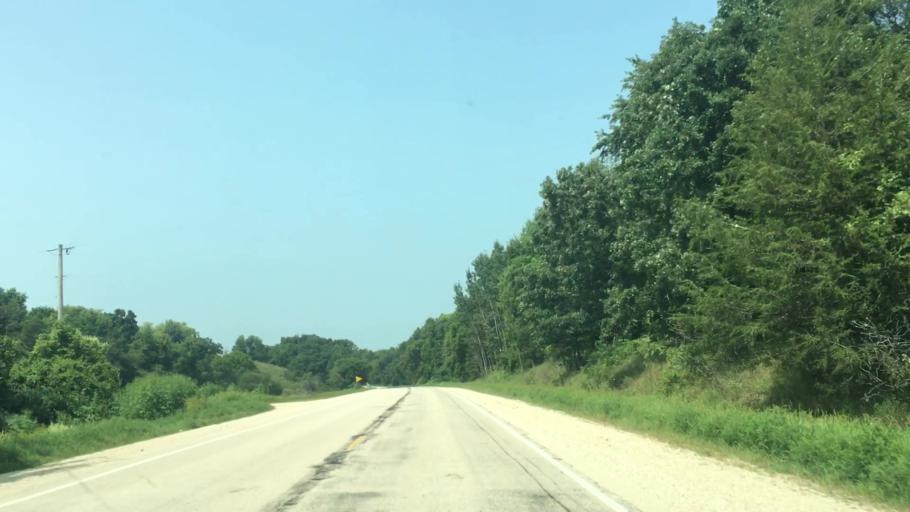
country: US
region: Iowa
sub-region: Fayette County
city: West Union
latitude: 43.0730
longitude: -91.8389
